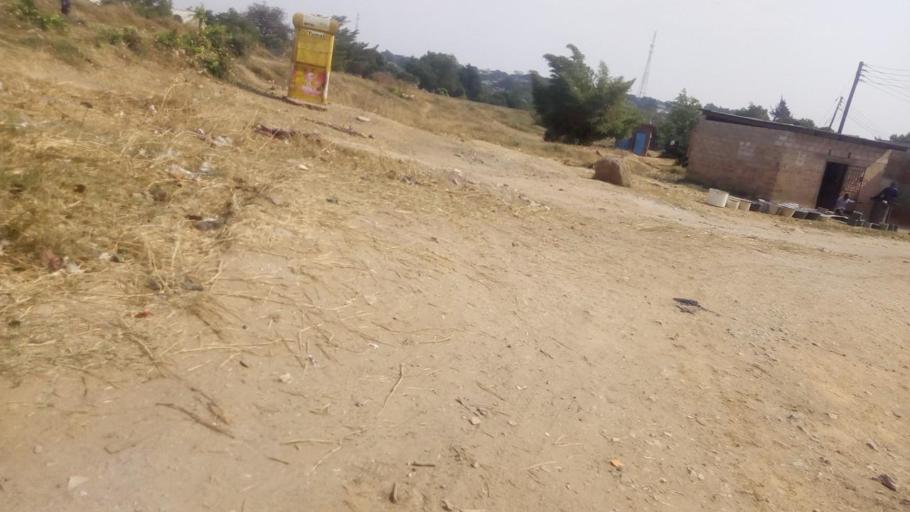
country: ZM
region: Lusaka
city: Lusaka
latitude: -15.3610
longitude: 28.3050
